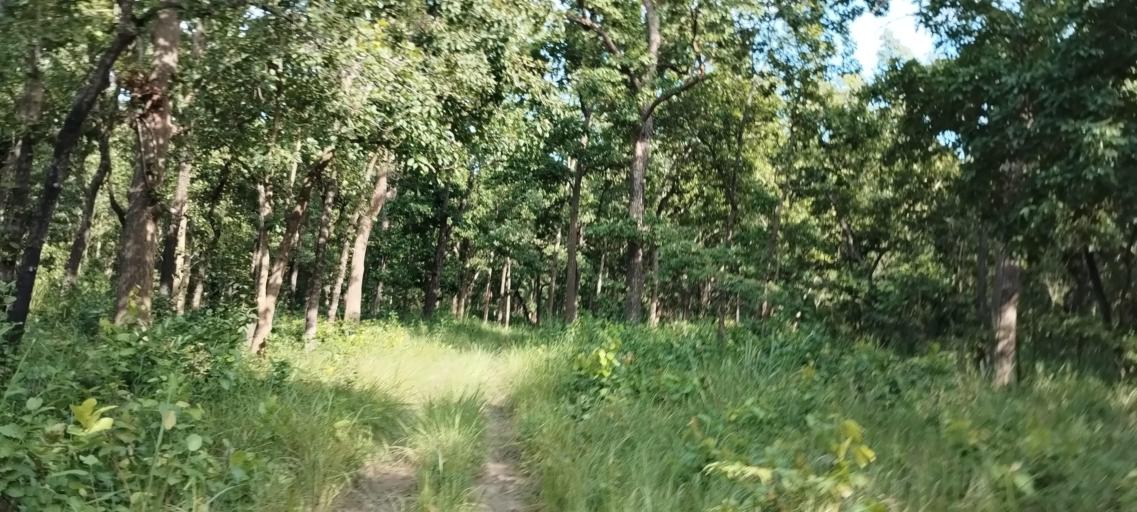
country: NP
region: Far Western
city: Tikapur
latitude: 28.5558
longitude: 81.2682
